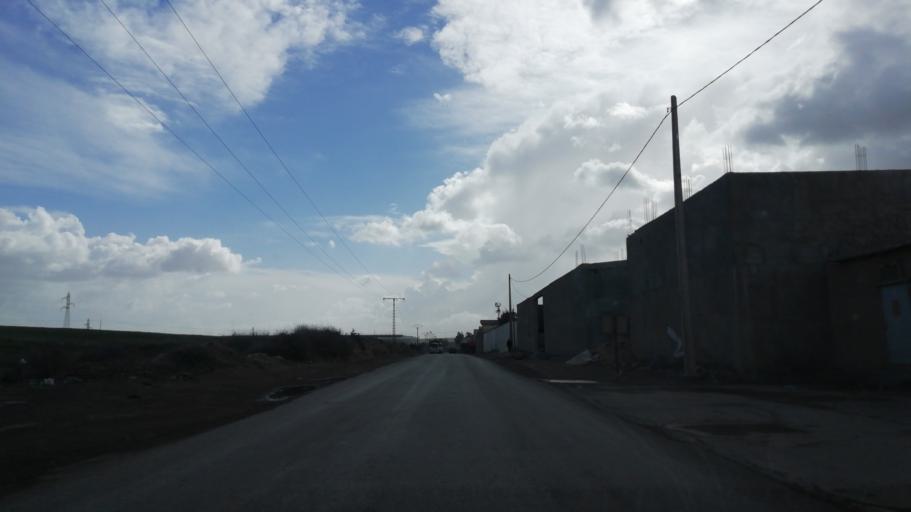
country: DZ
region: Oran
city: Sidi ech Chahmi
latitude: 35.6449
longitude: -0.5578
